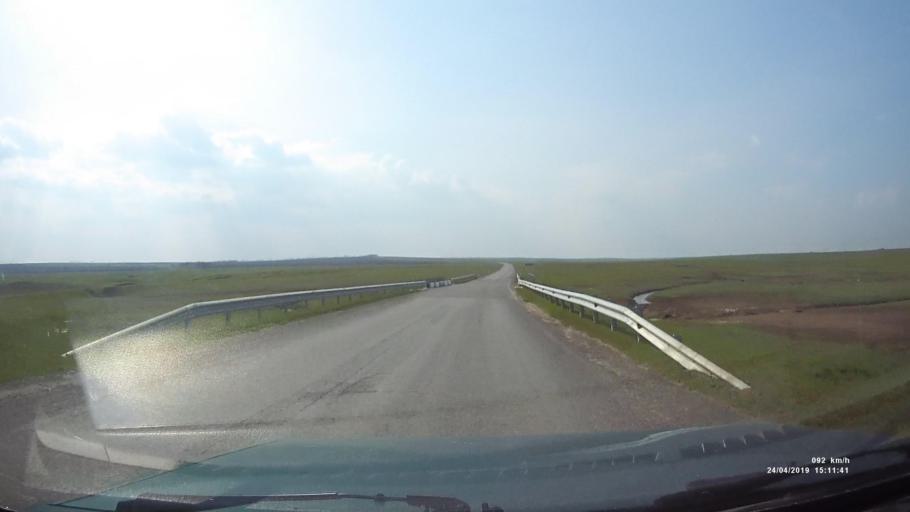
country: RU
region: Rostov
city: Remontnoye
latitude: 46.5441
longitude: 43.3166
